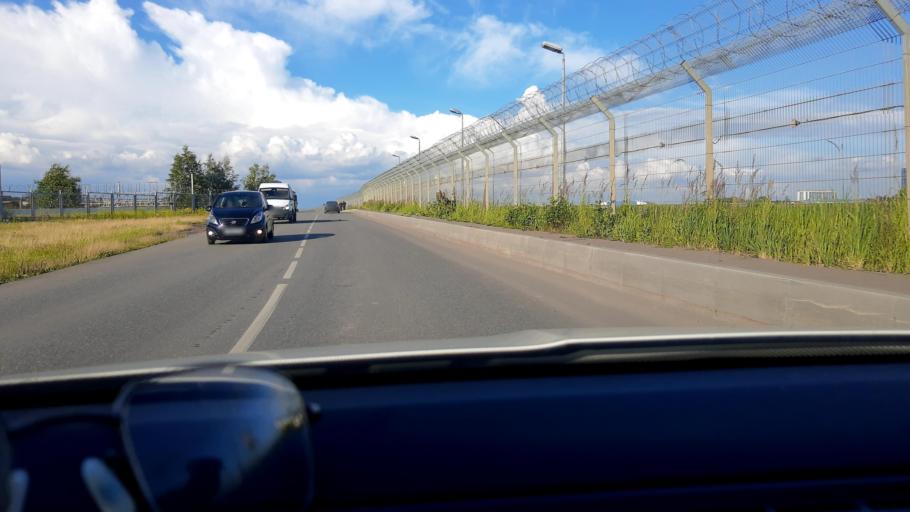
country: RU
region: Moskovskaya
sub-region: Leninskiy Rayon
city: Vnukovo
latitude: 55.6121
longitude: 37.2724
